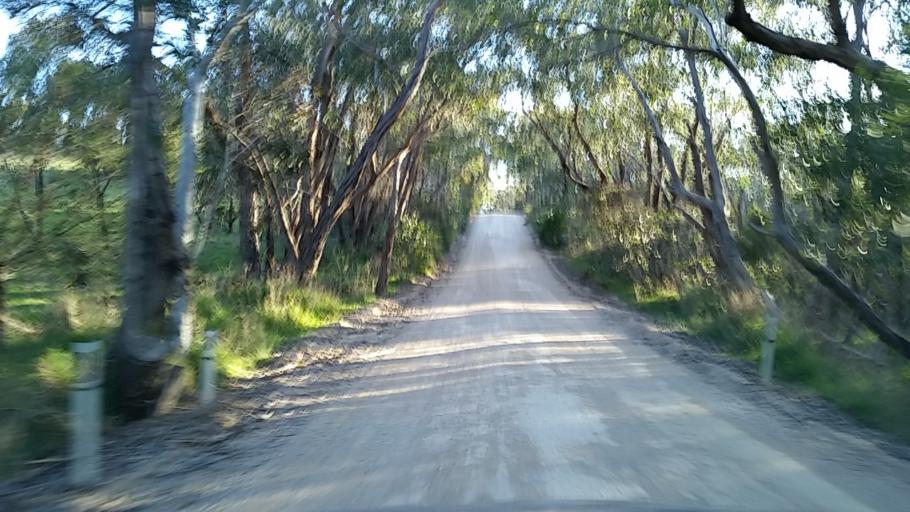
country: AU
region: South Australia
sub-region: Alexandrina
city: Mount Compass
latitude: -35.3018
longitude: 138.6793
